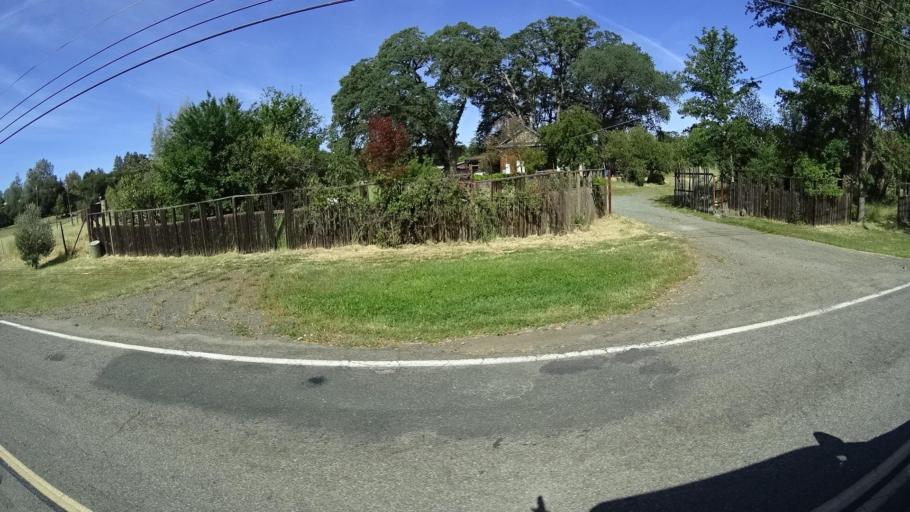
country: US
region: California
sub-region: Lake County
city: Kelseyville
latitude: 38.9591
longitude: -122.8384
